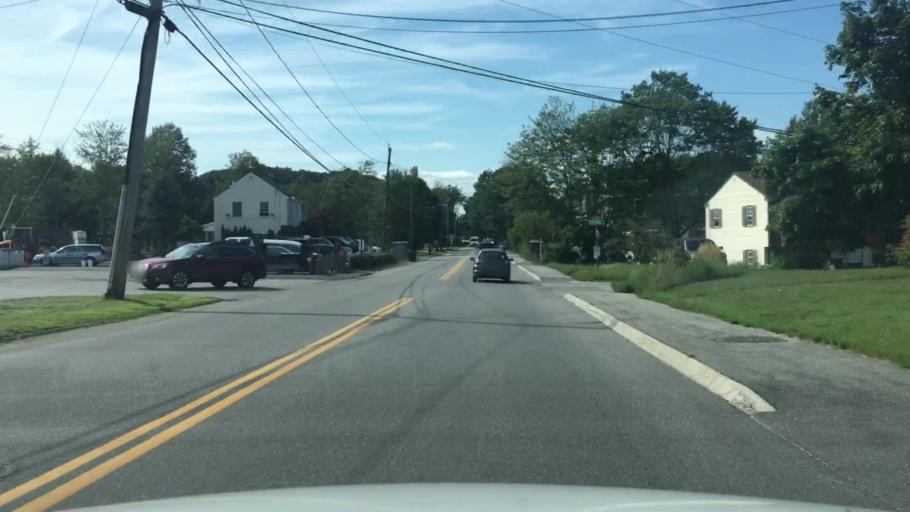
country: US
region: Maine
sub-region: Cumberland County
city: South Portland Gardens
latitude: 43.6297
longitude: -70.3023
